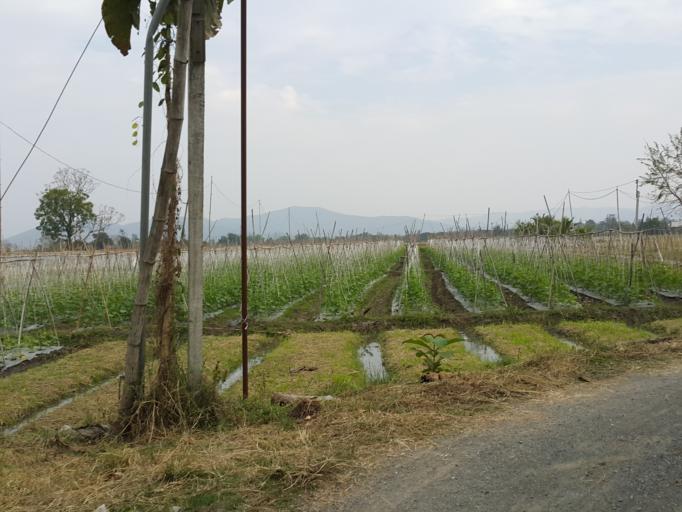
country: TH
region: Chiang Mai
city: San Kamphaeng
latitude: 18.8255
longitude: 99.1461
